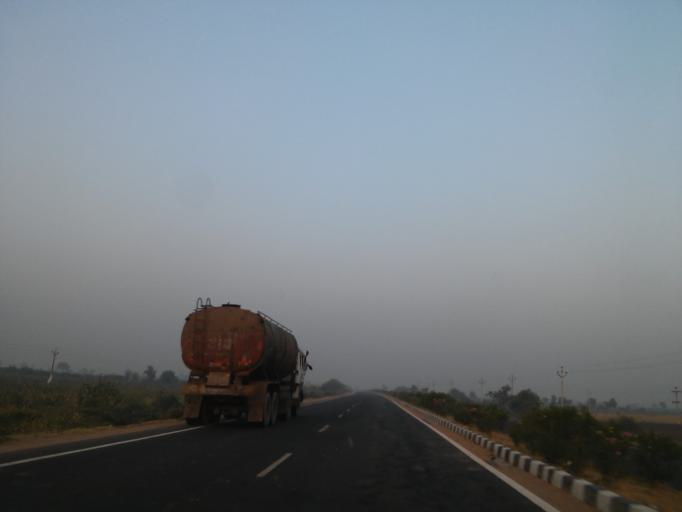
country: IN
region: Gujarat
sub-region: Surendranagar
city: Halvad
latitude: 23.0138
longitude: 71.0321
